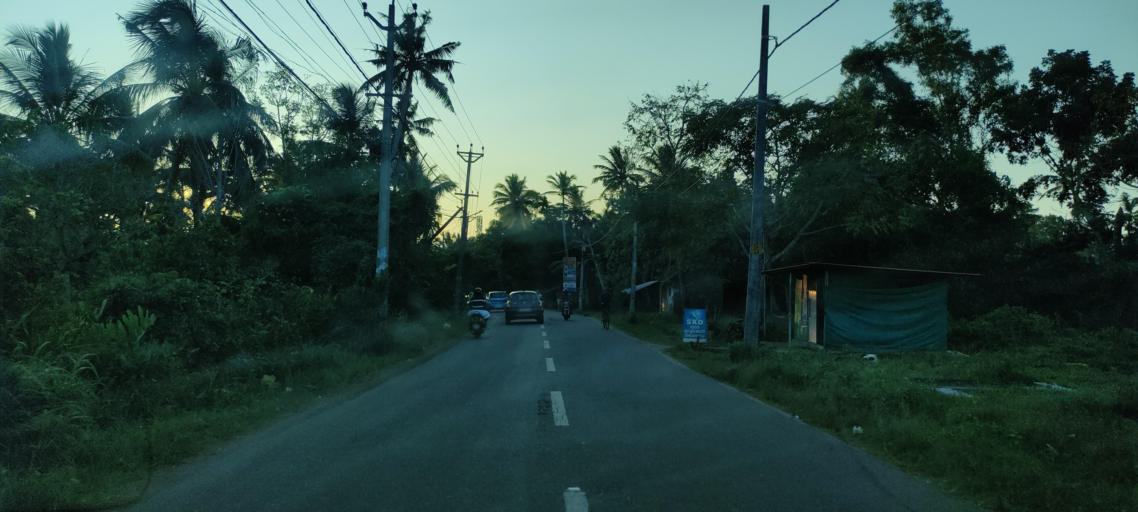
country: IN
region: Kerala
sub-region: Alappuzha
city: Kayankulam
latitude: 9.2583
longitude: 76.4285
